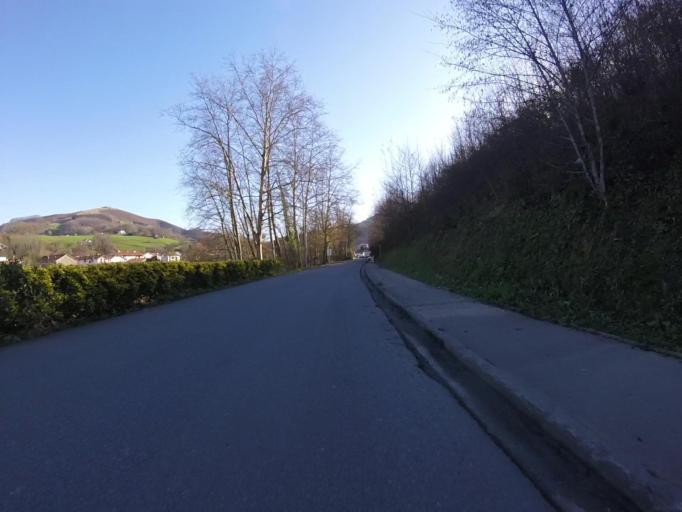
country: ES
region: Navarre
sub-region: Provincia de Navarra
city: Bera
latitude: 43.2774
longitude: -1.6906
